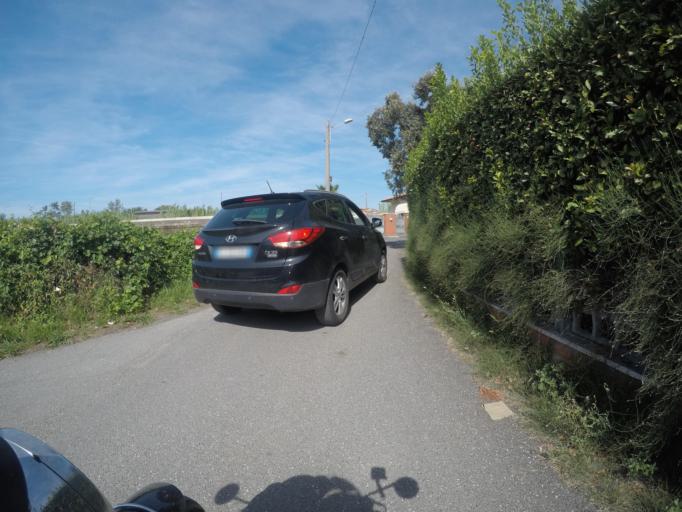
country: IT
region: Liguria
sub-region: Provincia di La Spezia
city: Casano-Dogana-Isola
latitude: 44.0614
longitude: 10.0309
